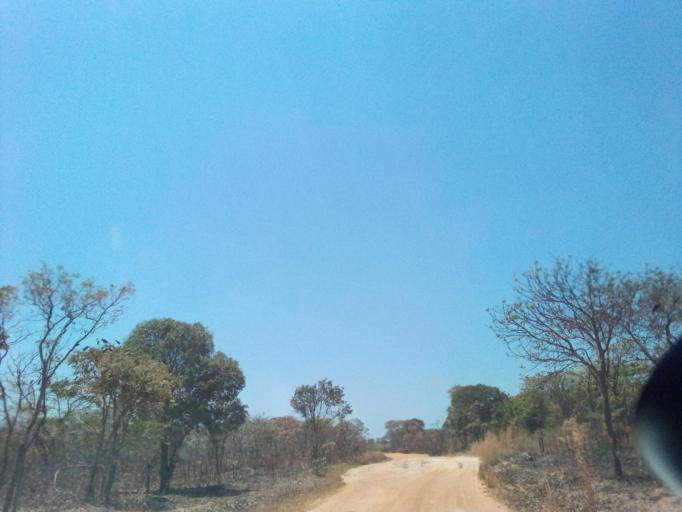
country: ZM
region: Northern
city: Mpika
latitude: -12.2538
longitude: 30.6803
